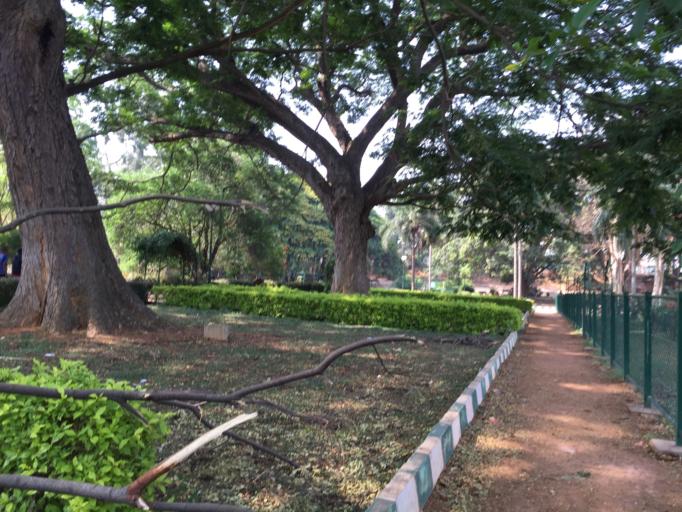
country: IN
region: Karnataka
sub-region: Bangalore Urban
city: Bangalore
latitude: 12.9486
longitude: 77.5849
